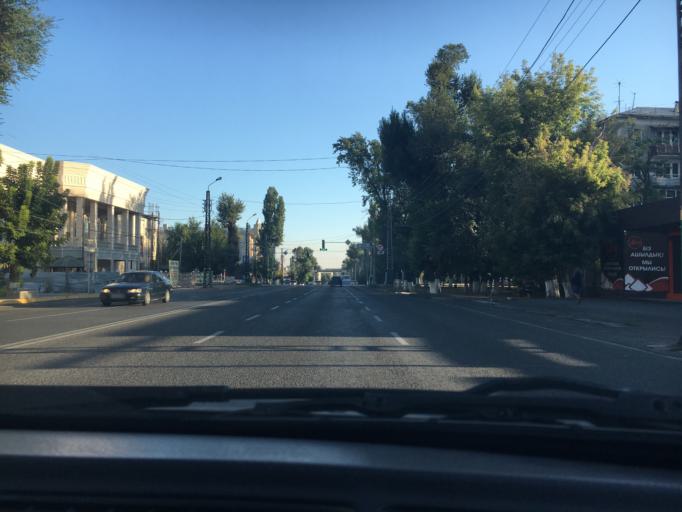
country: KZ
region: Zhambyl
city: Taraz
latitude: 42.8963
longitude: 71.3604
